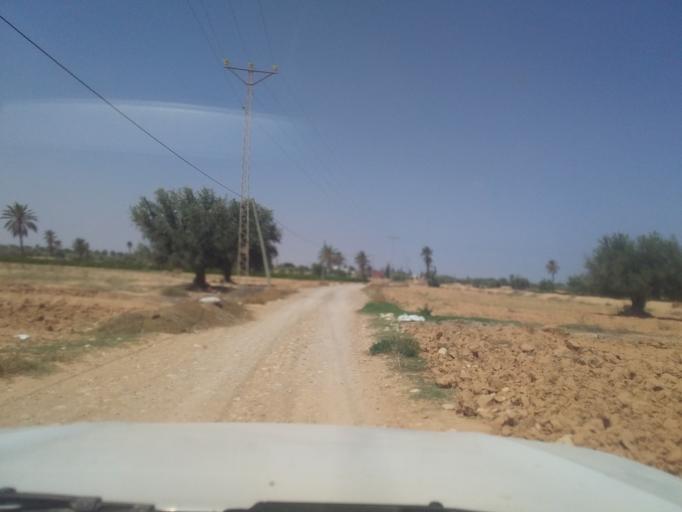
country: TN
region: Qabis
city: Matmata
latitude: 33.5953
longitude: 10.2832
